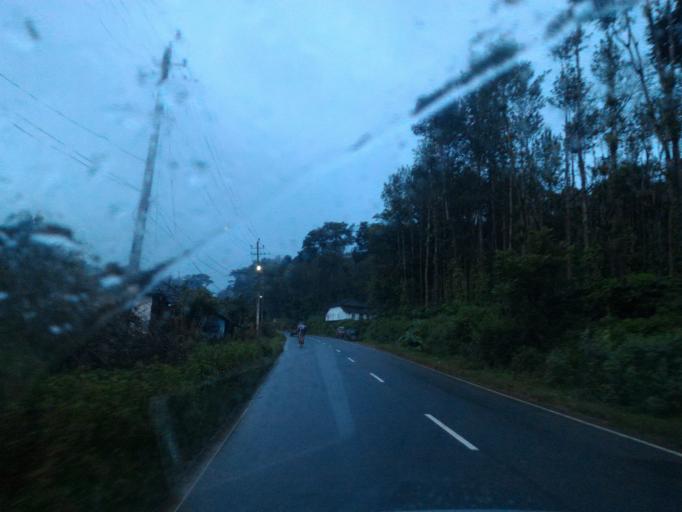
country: IN
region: Karnataka
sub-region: Kodagu
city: Suntikoppa
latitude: 12.4393
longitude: 75.8099
